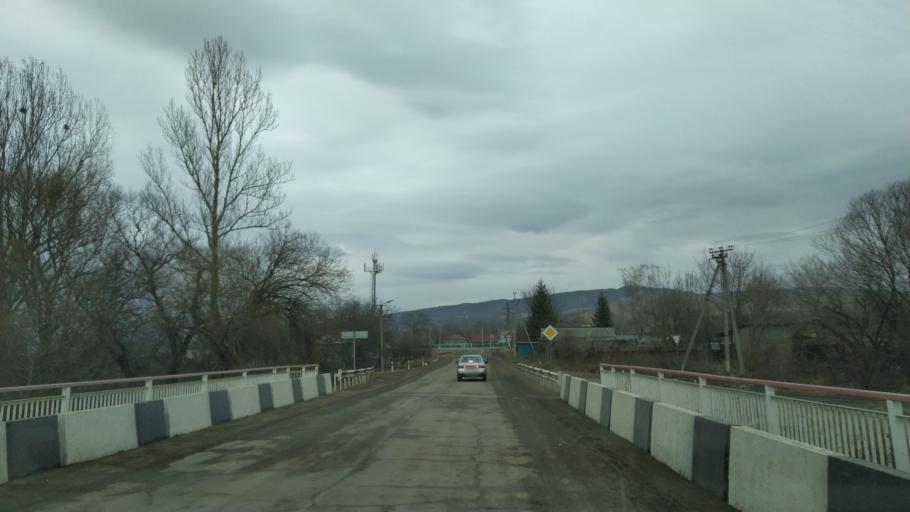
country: RU
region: Krasnodarskiy
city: Peredovaya
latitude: 44.1181
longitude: 41.4698
